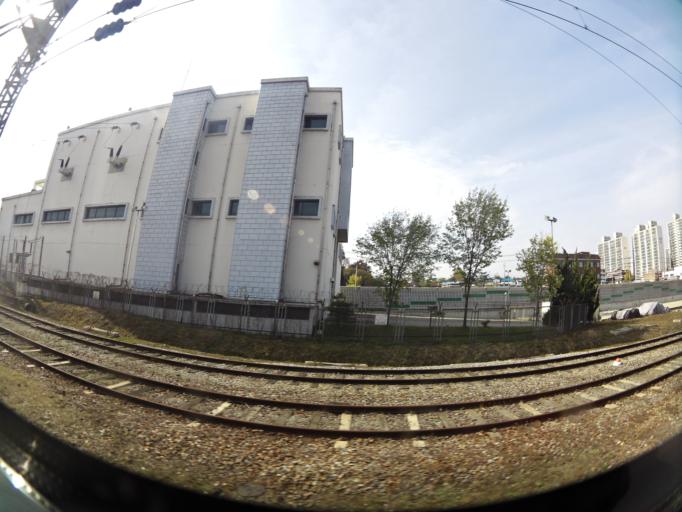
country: KR
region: Daejeon
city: Songgang-dong
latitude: 36.5995
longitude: 127.2958
